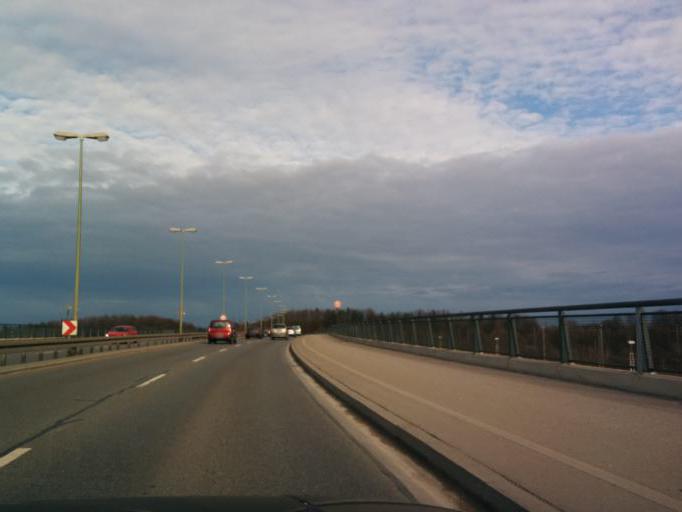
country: DE
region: Bavaria
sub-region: Upper Bavaria
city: Karlsfeld
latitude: 48.1956
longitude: 11.4954
